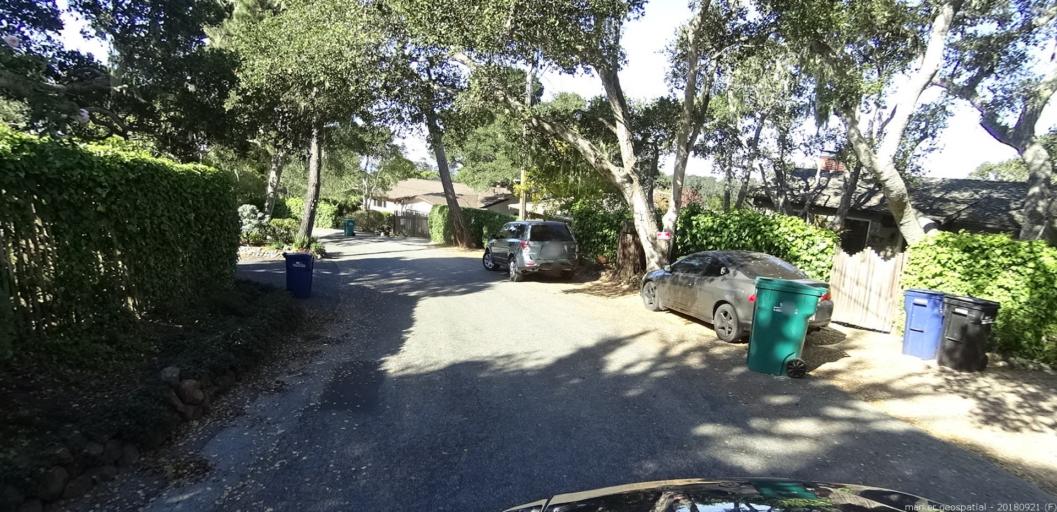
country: US
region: California
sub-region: Monterey County
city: Carmel-by-the-Sea
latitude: 36.5693
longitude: -121.9191
